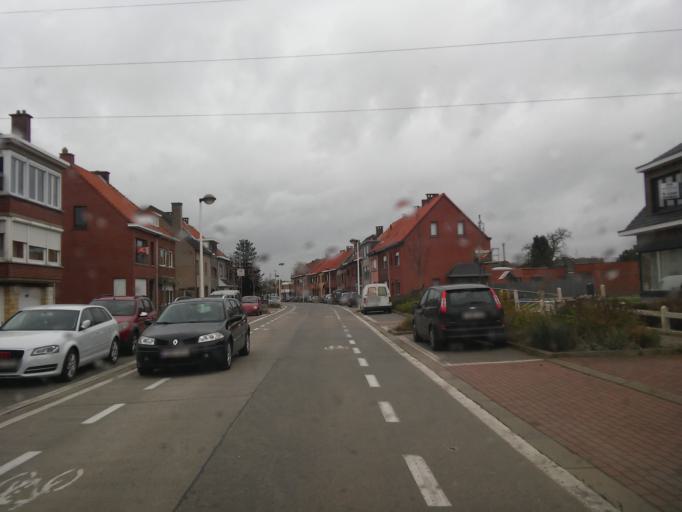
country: BE
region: Flanders
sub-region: Provincie Oost-Vlaanderen
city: Kruibeke
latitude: 51.1368
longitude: 4.2944
